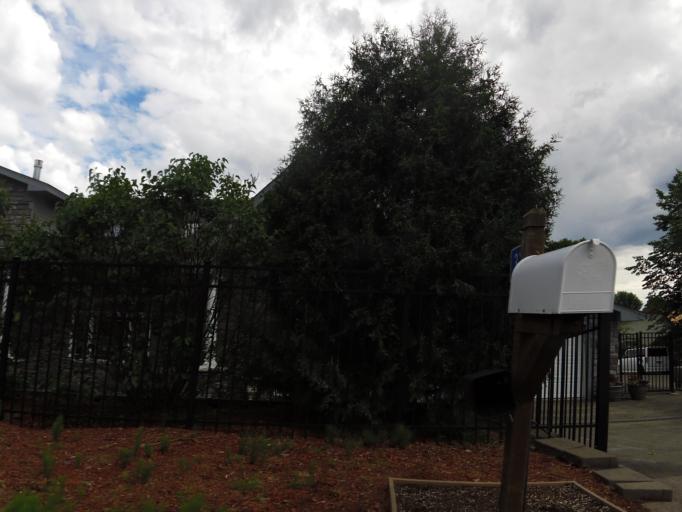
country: US
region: Minnesota
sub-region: Scott County
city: Prior Lake
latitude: 44.7525
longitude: -93.4565
